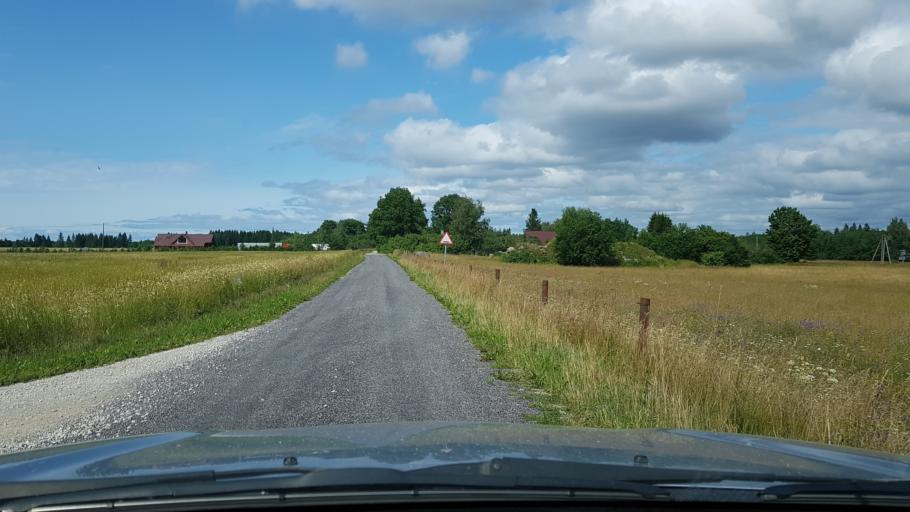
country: EE
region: Ida-Virumaa
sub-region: Narva-Joesuu linn
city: Narva-Joesuu
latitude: 59.3698
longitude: 27.9539
